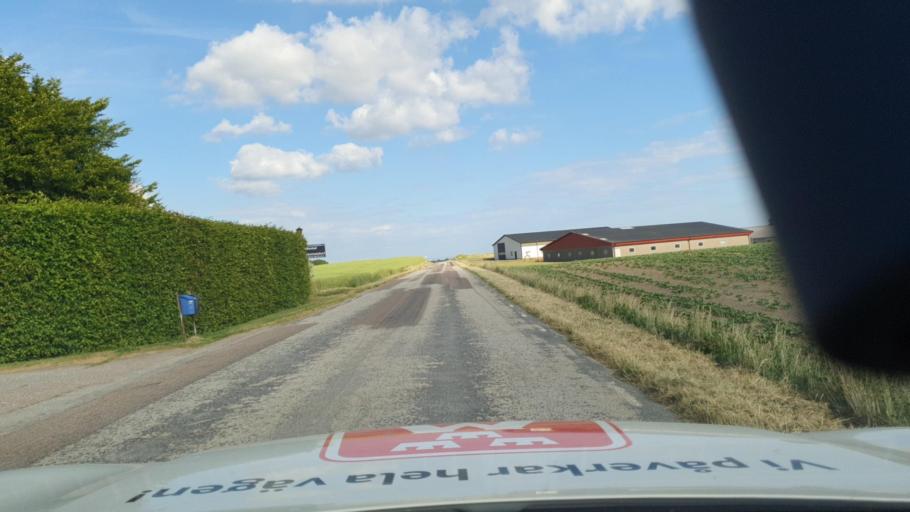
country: SE
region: Skane
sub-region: Skurups Kommun
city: Rydsgard
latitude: 55.4422
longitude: 13.6593
